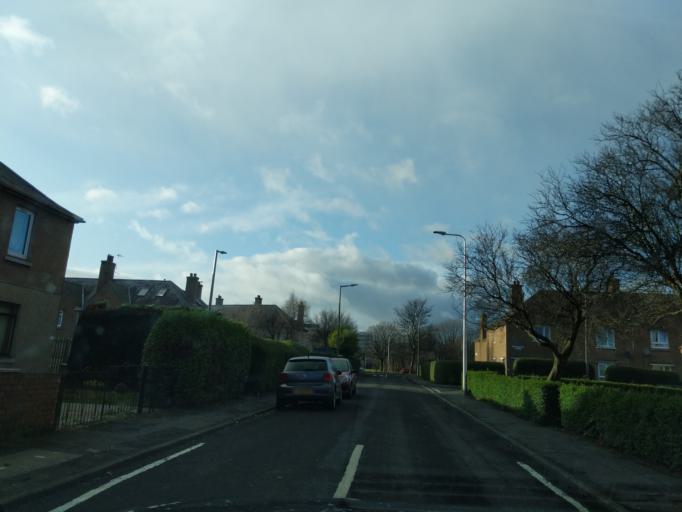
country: GB
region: Scotland
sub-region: Edinburgh
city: Colinton
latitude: 55.9281
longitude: -3.2821
